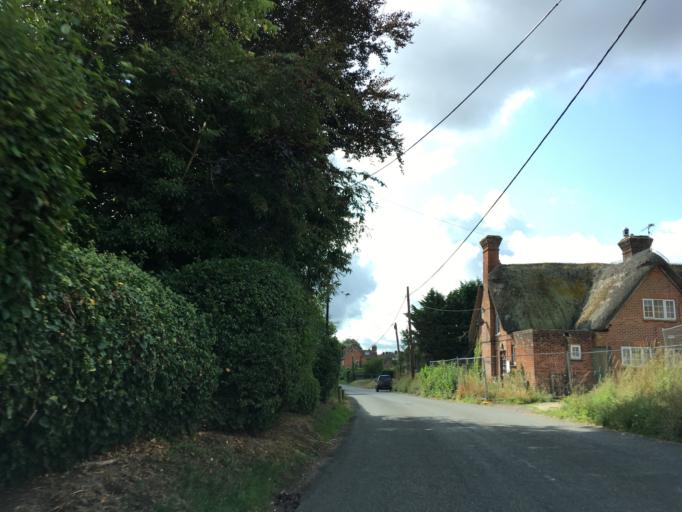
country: GB
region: England
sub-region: Hampshire
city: Overton
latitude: 51.2146
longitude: -1.3752
